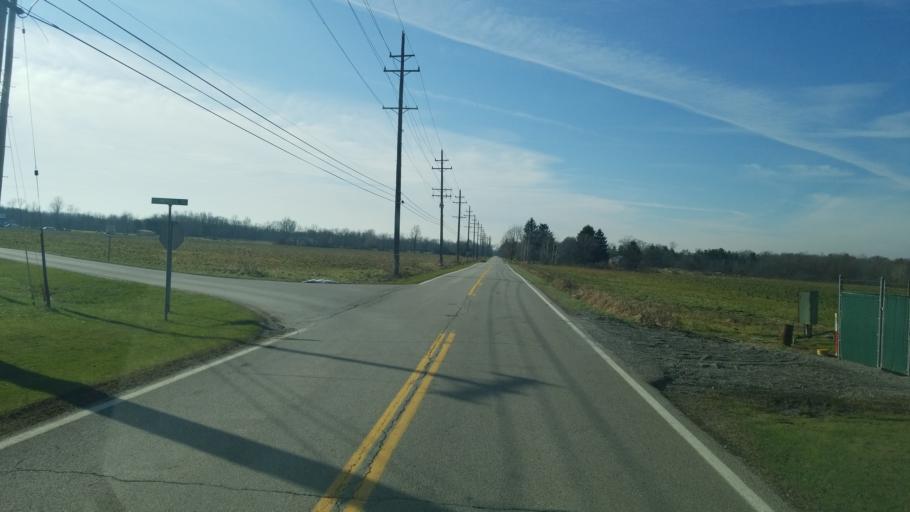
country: US
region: Ohio
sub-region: Ashtabula County
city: Jefferson
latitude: 41.7369
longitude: -80.7980
